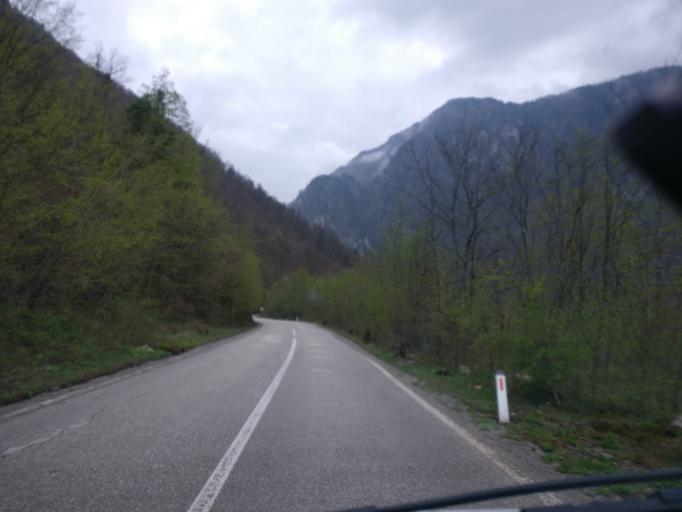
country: ME
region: Opstina Pluzine
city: Pluzine
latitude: 43.3142
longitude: 18.8566
